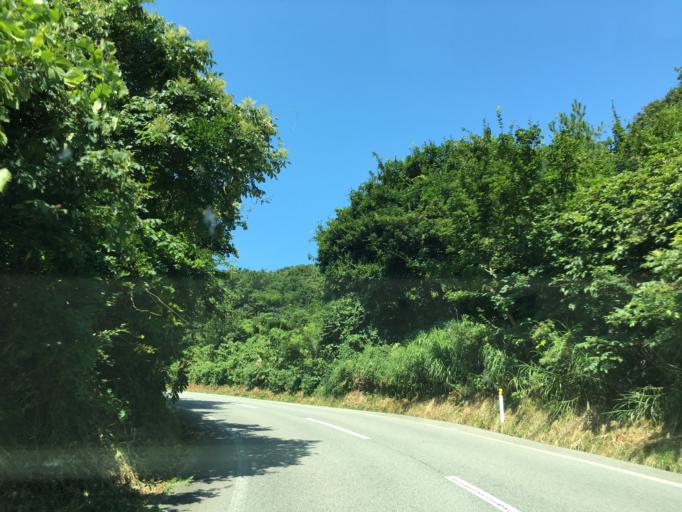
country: JP
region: Akita
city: Tenno
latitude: 39.9161
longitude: 139.7206
